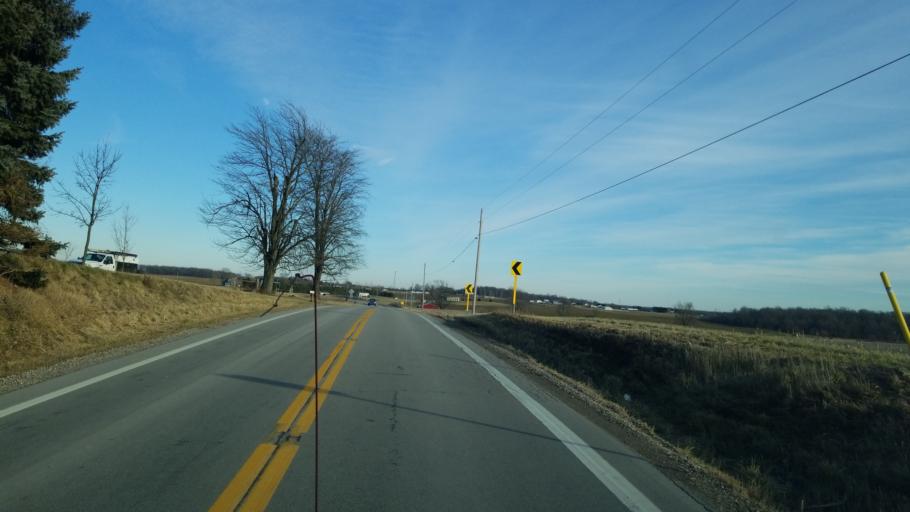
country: US
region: Ohio
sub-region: Huron County
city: Greenwich
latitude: 41.1013
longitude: -82.5297
